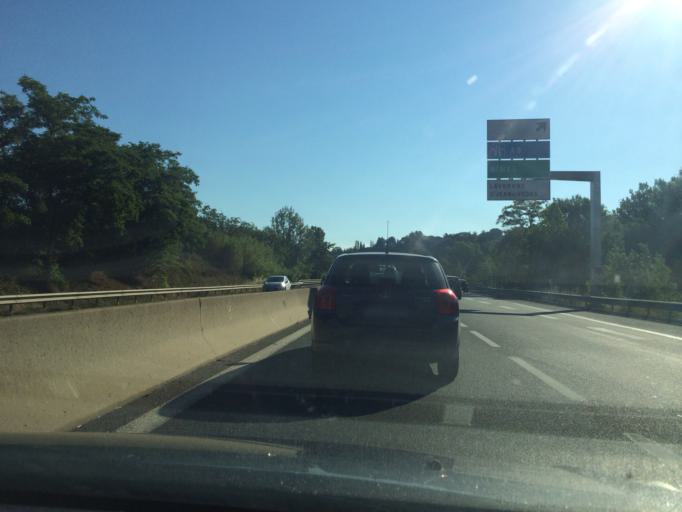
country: FR
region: Languedoc-Roussillon
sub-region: Departement de l'Herault
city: Juvignac
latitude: 43.6066
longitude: 3.8183
